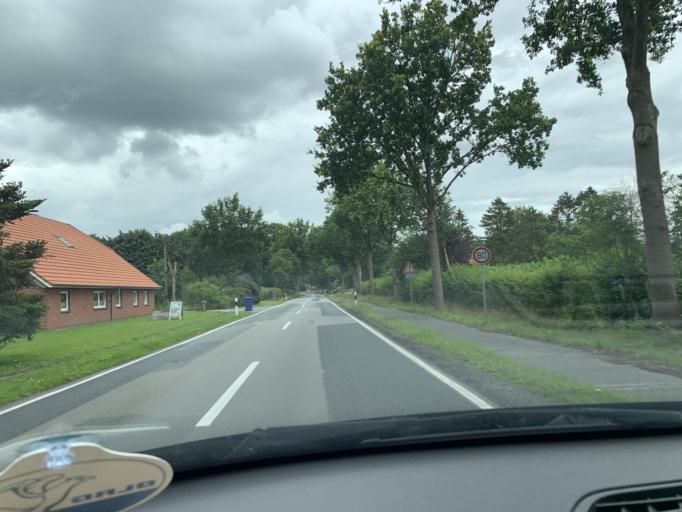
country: DE
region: Lower Saxony
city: Edewecht
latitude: 53.1395
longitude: 7.8782
